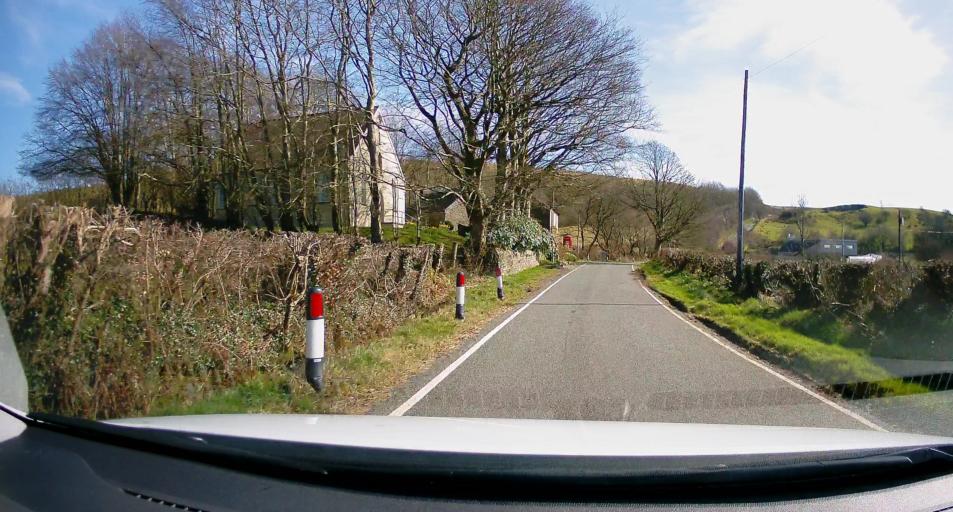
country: GB
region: Wales
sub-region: County of Ceredigion
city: Lledrod
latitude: 52.2839
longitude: -4.0602
